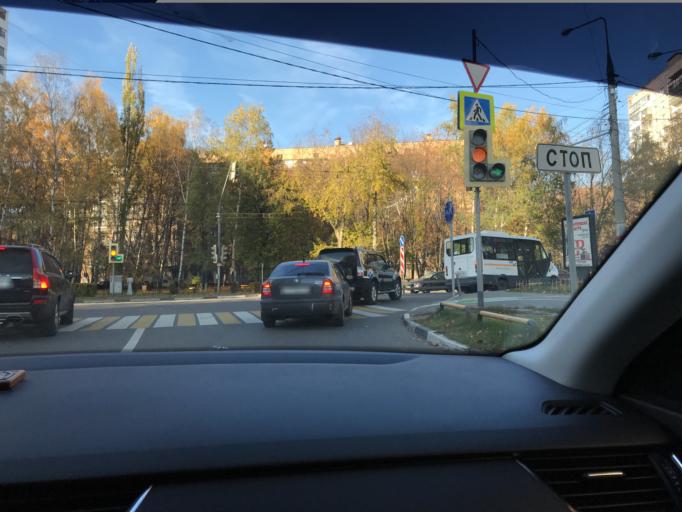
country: RU
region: Moscow
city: Khimki
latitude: 55.8868
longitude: 37.4261
